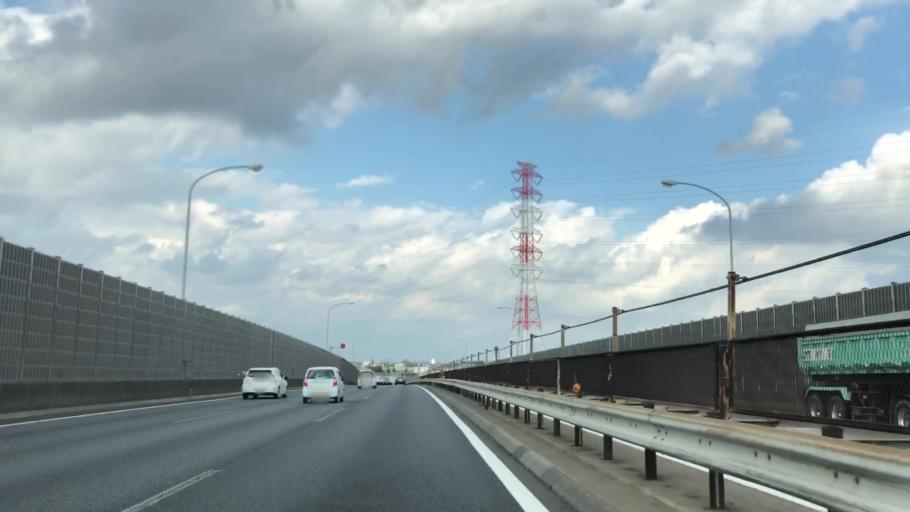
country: JP
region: Chiba
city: Nagareyama
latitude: 35.8461
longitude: 139.8724
